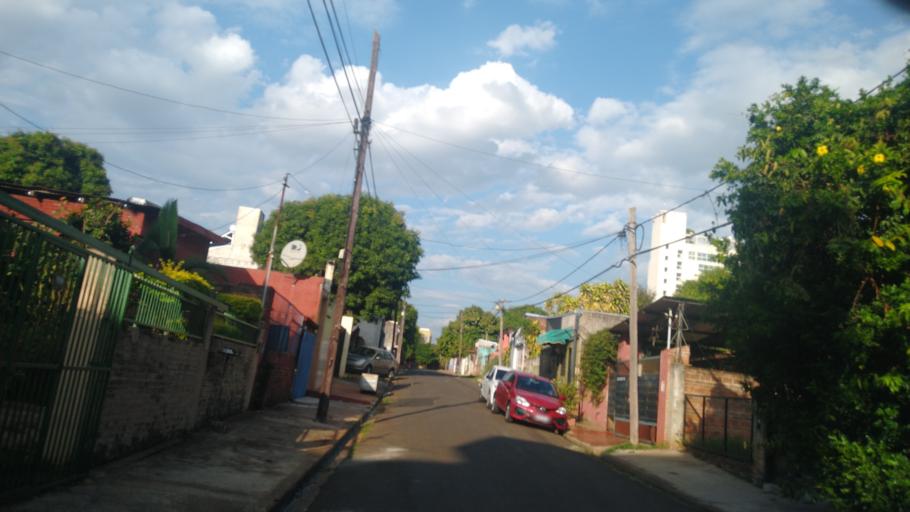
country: AR
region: Misiones
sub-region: Departamento de Capital
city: Posadas
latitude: -27.3812
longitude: -55.8896
